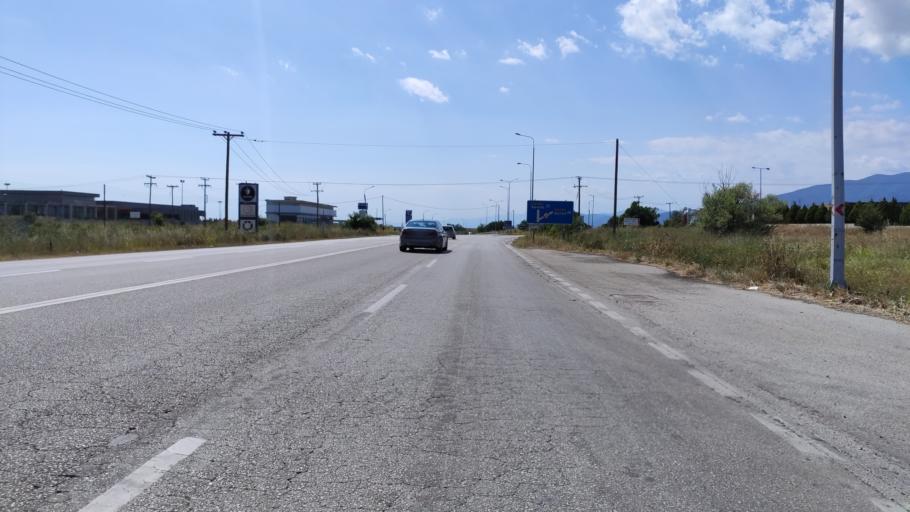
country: GR
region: East Macedonia and Thrace
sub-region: Nomos Rodopis
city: Komotini
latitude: 41.1085
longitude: 25.3519
